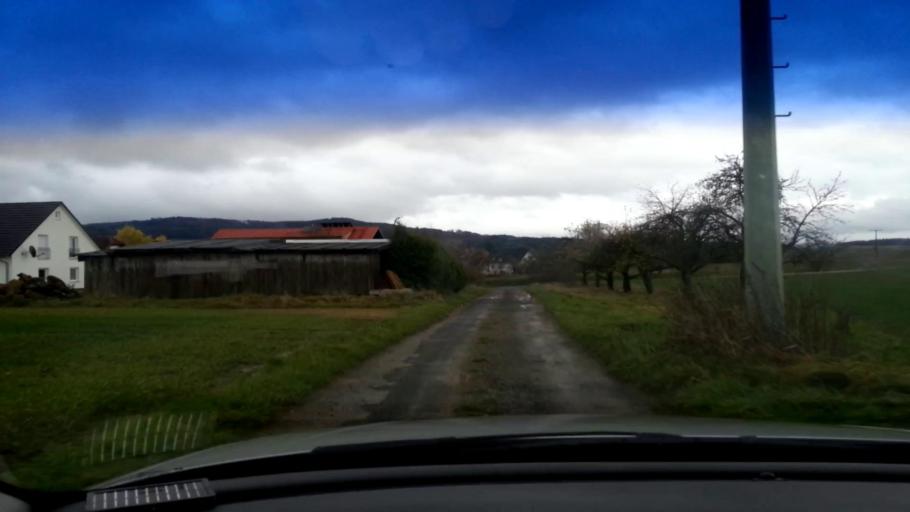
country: DE
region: Bavaria
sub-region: Upper Franconia
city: Ebensfeld
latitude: 50.0353
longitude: 10.9974
